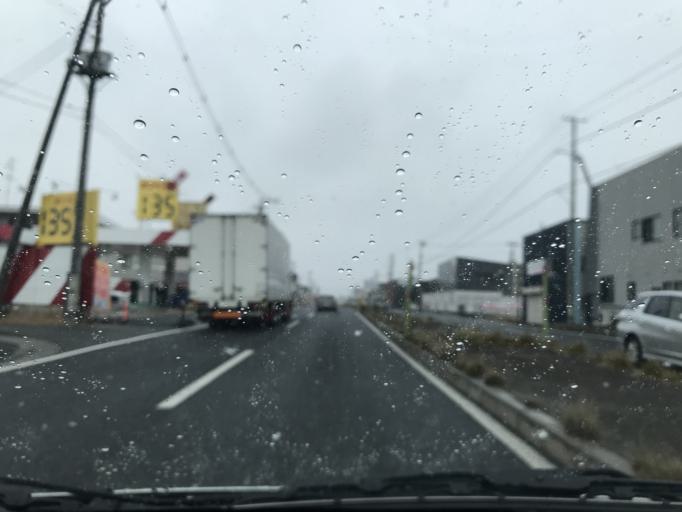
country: JP
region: Iwate
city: Kitakami
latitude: 39.2886
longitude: 141.1041
